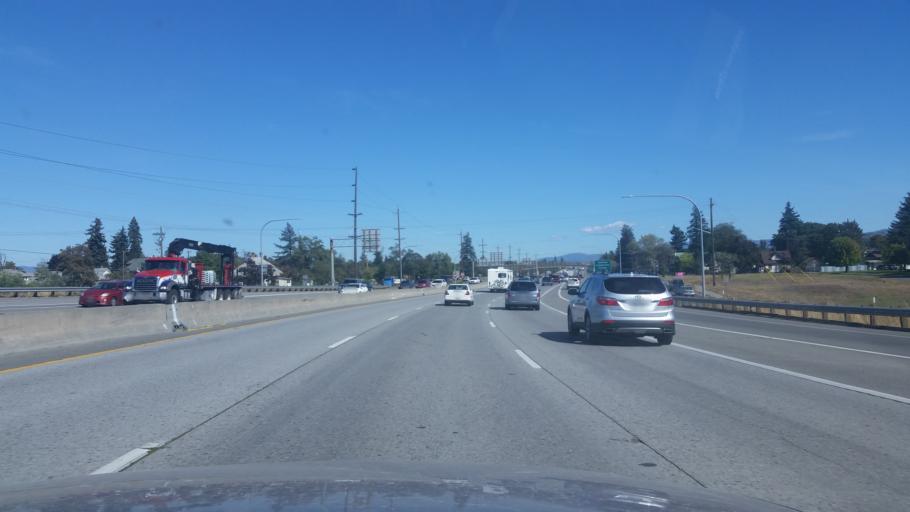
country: US
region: Washington
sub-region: Spokane County
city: Spokane
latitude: 47.6538
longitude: -117.3891
